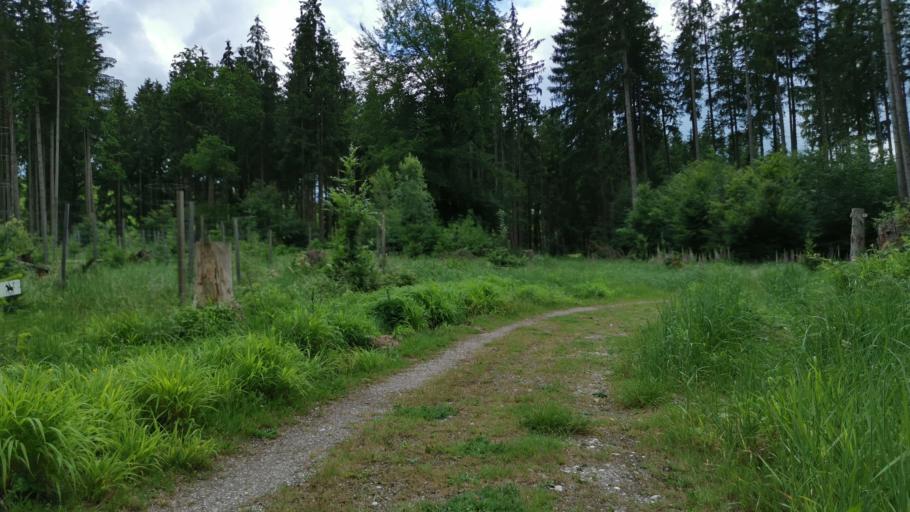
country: DE
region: Bavaria
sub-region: Upper Bavaria
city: Pullach im Isartal
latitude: 48.0573
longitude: 11.4978
